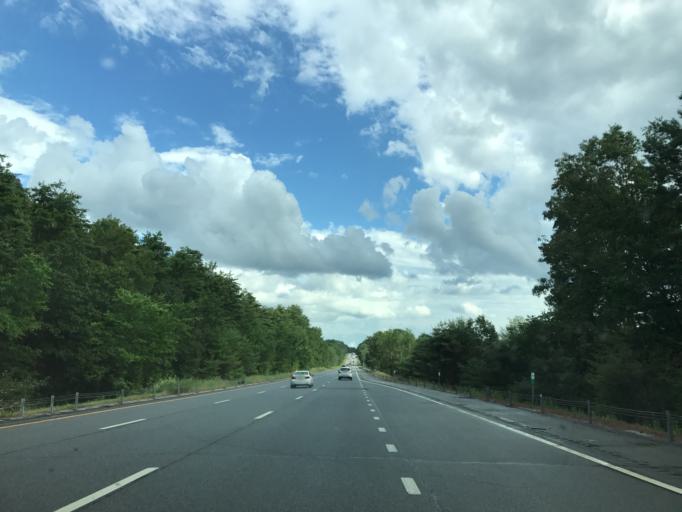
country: US
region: New York
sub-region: Warren County
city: Glens Falls North
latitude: 43.3540
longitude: -73.7018
